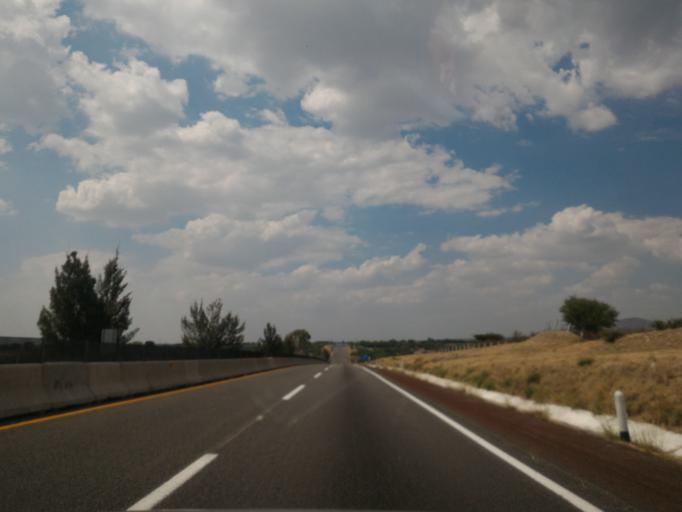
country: MX
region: Jalisco
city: Encarnacion de Diaz
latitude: 21.5730
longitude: -102.2744
